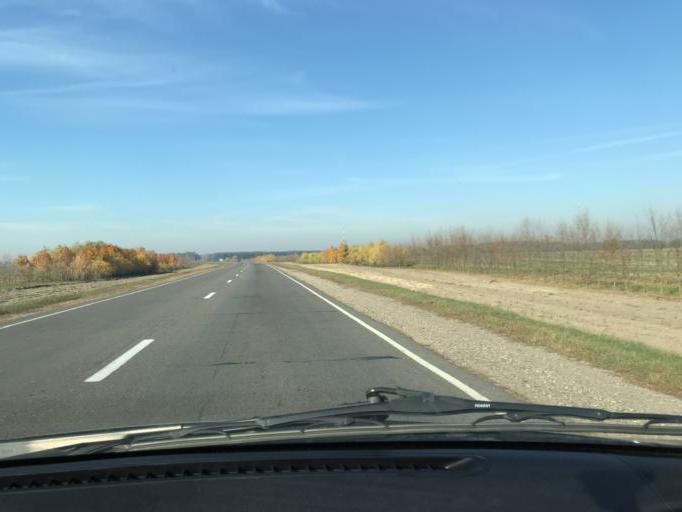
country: BY
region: Brest
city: Luninyets
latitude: 52.2740
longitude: 26.9811
